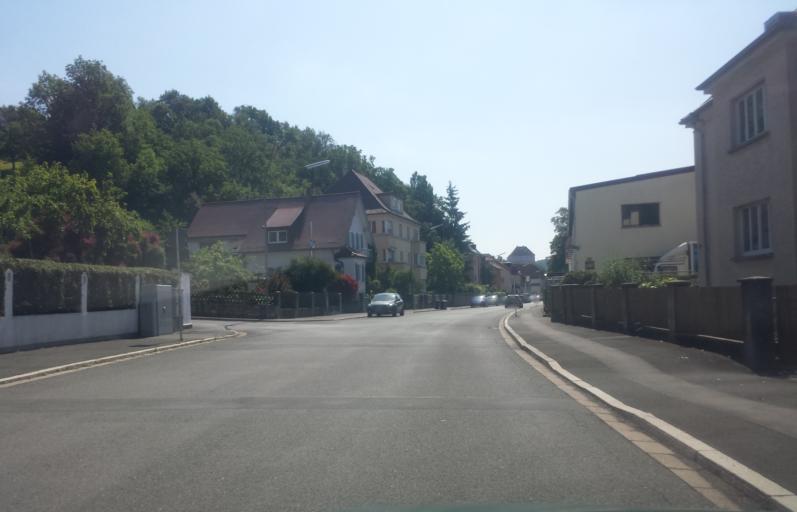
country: DE
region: Bavaria
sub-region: Upper Franconia
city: Burgkunstadt
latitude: 50.1436
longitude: 11.2418
